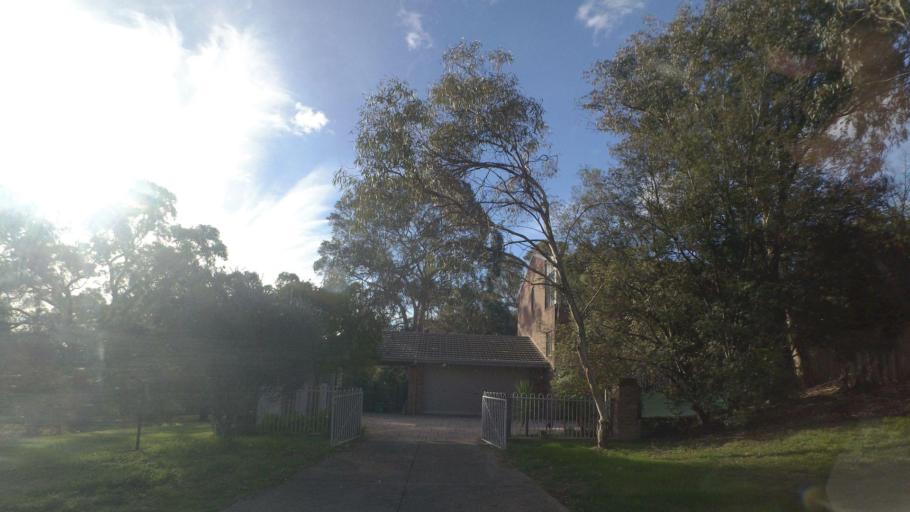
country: AU
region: Victoria
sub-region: Banyule
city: Yallambie
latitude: -37.7285
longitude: 145.0839
